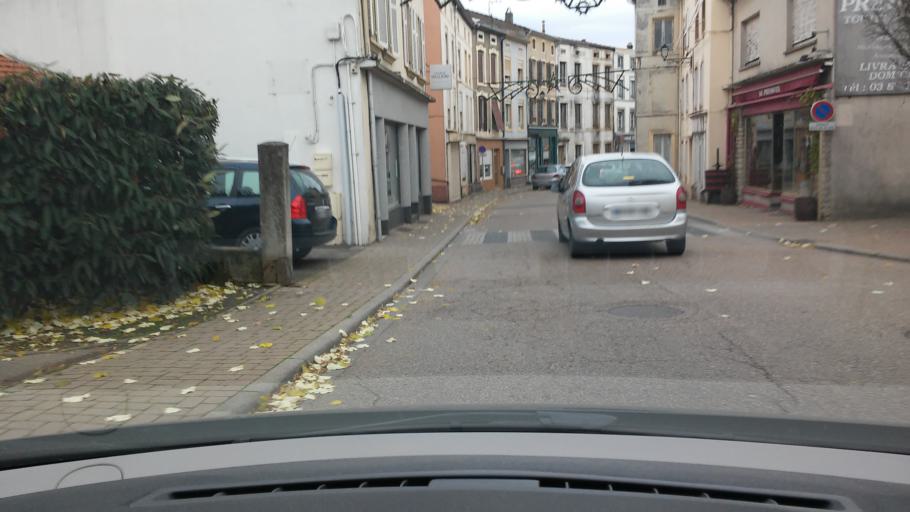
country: FR
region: Lorraine
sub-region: Departement de la Moselle
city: Boulay-Moselle
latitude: 49.1824
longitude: 6.4959
